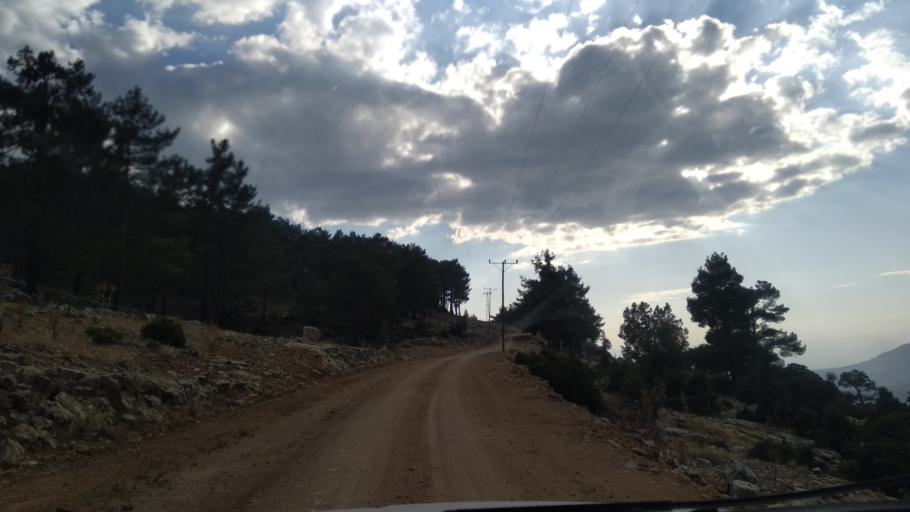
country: TR
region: Mersin
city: Sarikavak
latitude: 36.5984
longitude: 33.6998
